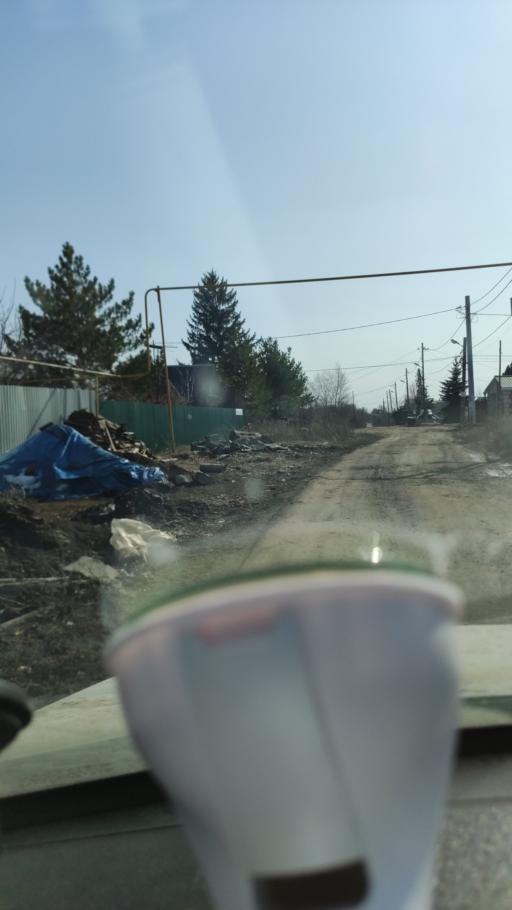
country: RU
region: Samara
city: Petra-Dubrava
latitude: 53.2581
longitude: 50.3491
